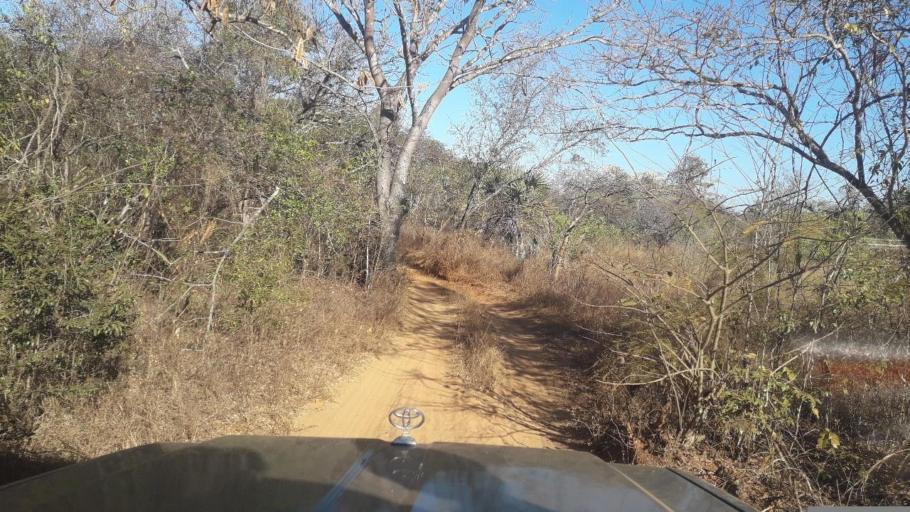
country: MG
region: Boeny
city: Sitampiky
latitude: -16.4180
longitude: 45.6116
